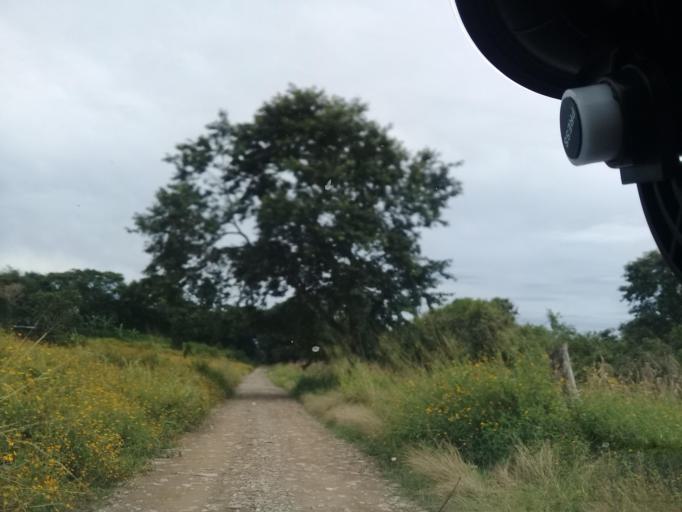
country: MX
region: Hidalgo
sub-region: Huejutla de Reyes
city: Chalahuiyapa
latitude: 21.1706
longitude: -98.3727
